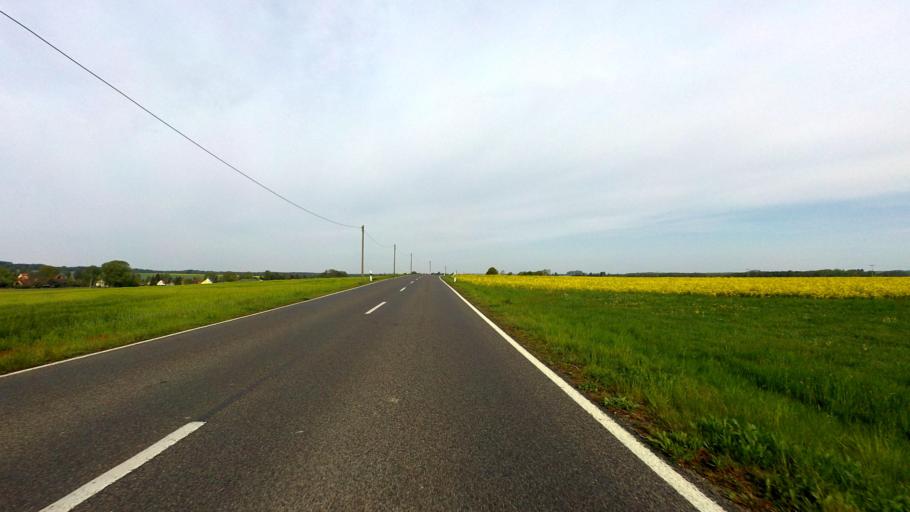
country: DE
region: Saxony
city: Arnsdorf
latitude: 51.0797
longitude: 14.0310
